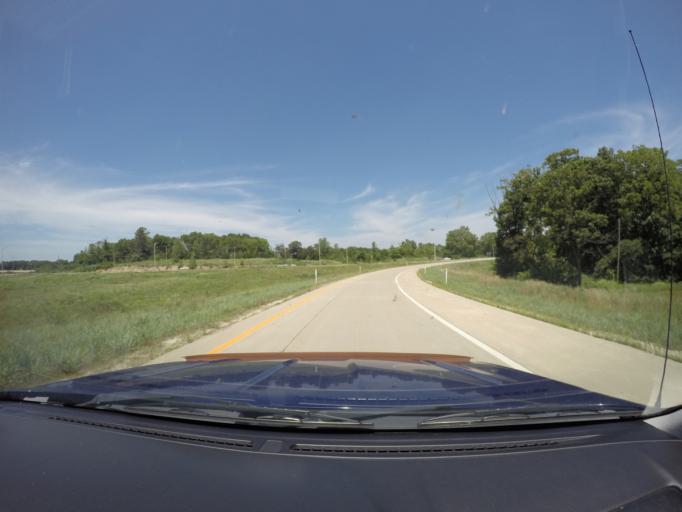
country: US
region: Kansas
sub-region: Leavenworth County
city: Basehor
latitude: 39.1149
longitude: -94.8914
